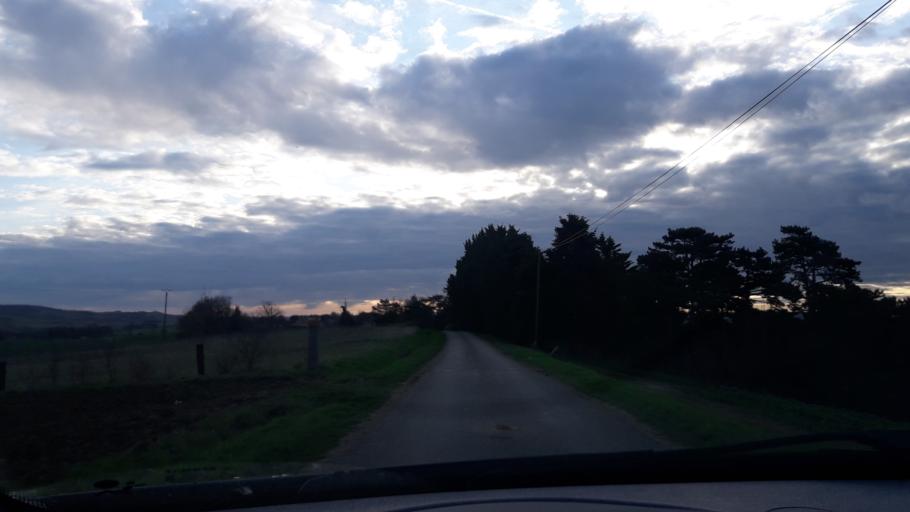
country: FR
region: Midi-Pyrenees
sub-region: Departement du Gers
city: Pujaudran
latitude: 43.6672
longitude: 1.0488
